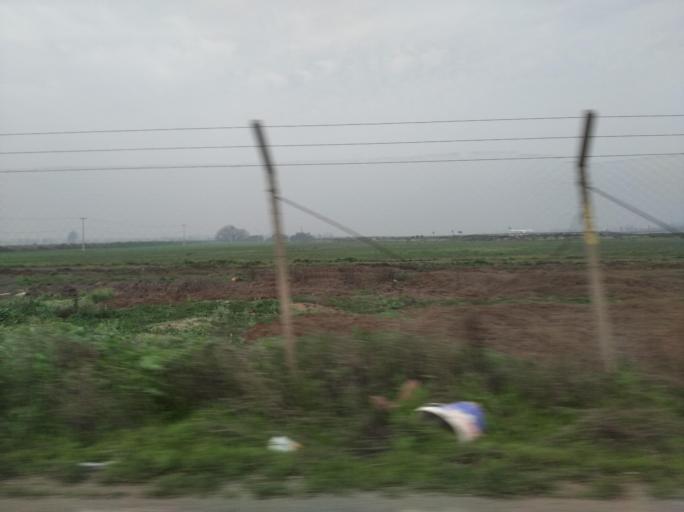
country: CL
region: Santiago Metropolitan
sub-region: Provincia de Chacabuco
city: Lampa
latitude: -33.3643
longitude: -70.7999
